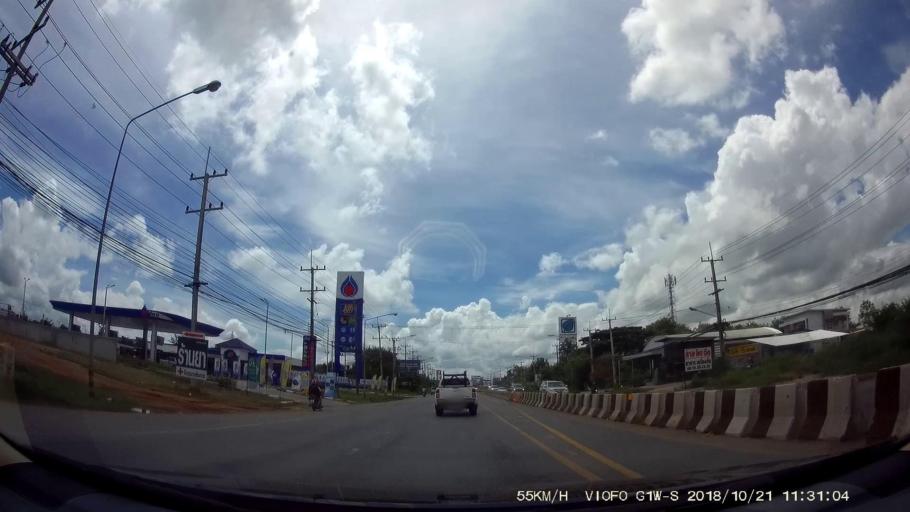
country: TH
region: Chaiyaphum
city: Chaiyaphum
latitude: 15.7723
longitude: 102.0259
